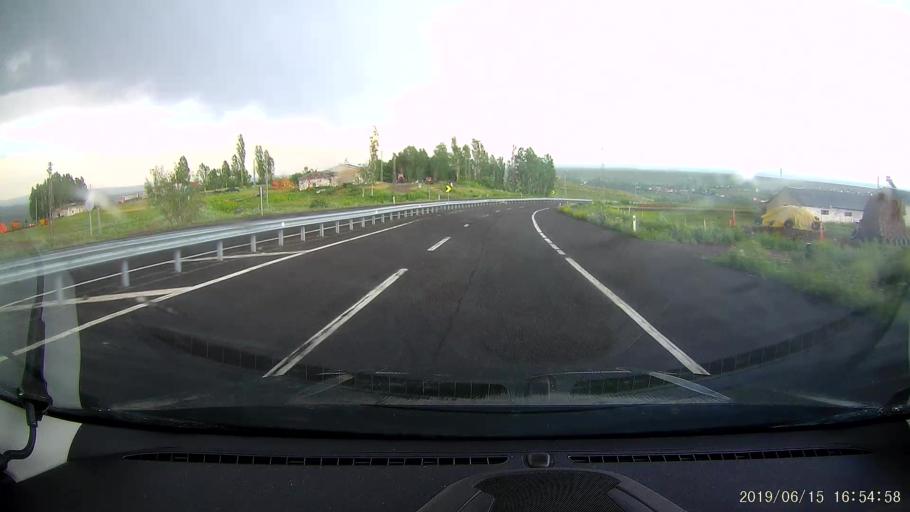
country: TR
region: Kars
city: Susuz
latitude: 40.7873
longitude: 43.1354
